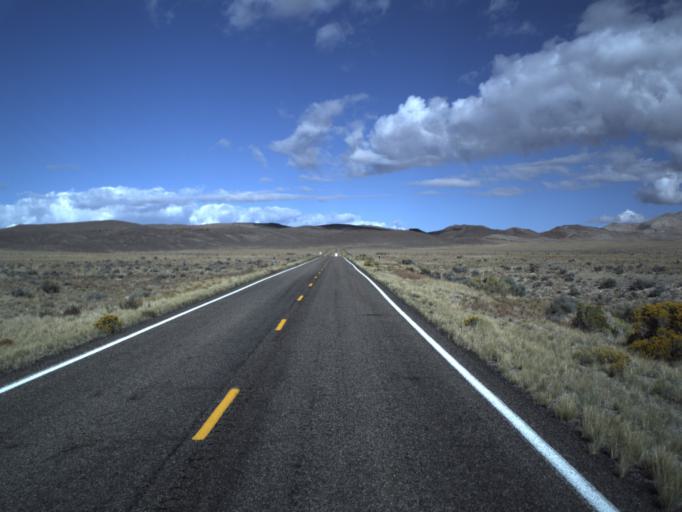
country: US
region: Utah
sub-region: Beaver County
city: Milford
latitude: 38.5855
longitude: -113.8137
